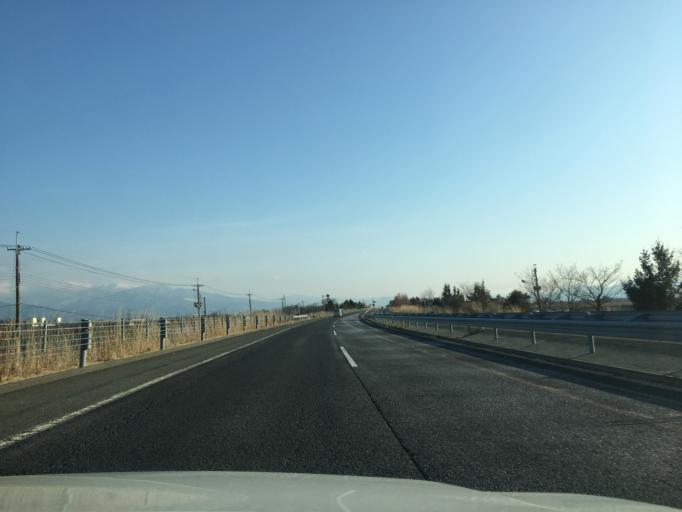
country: JP
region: Yamagata
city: Sagae
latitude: 38.3516
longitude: 140.2967
